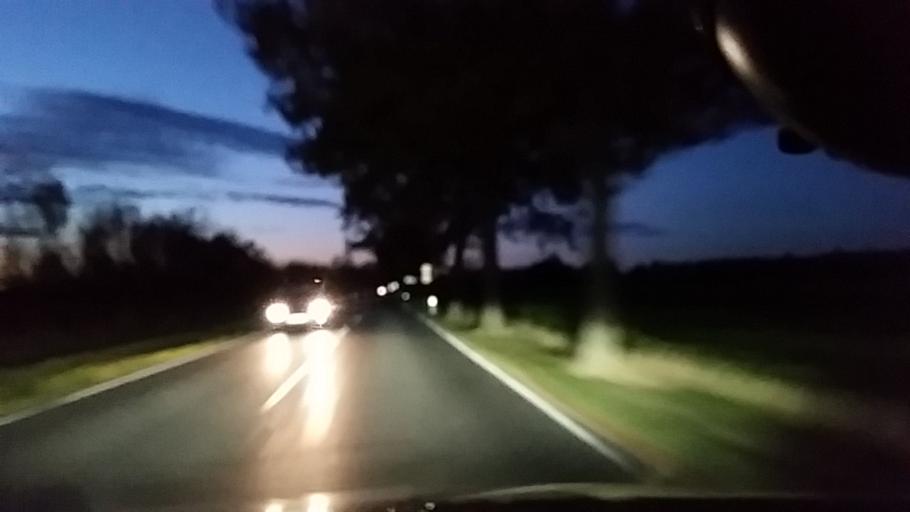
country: DE
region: Lower Saxony
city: Jembke
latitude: 52.4646
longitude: 10.7823
